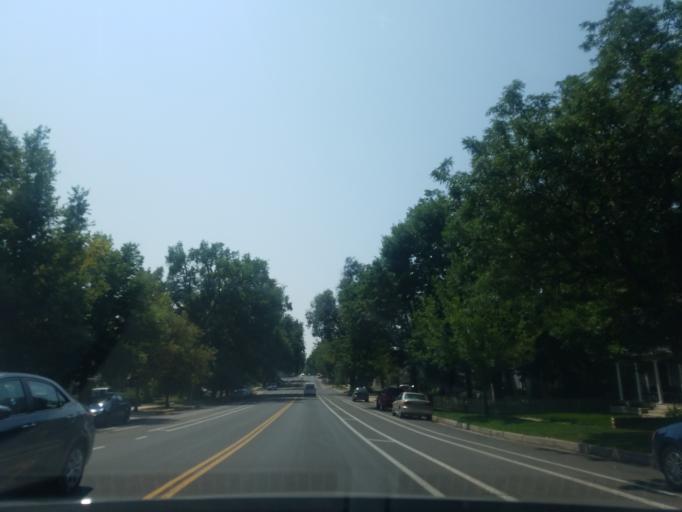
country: US
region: Colorado
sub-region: Larimer County
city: Fort Collins
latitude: 40.5765
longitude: -105.0756
